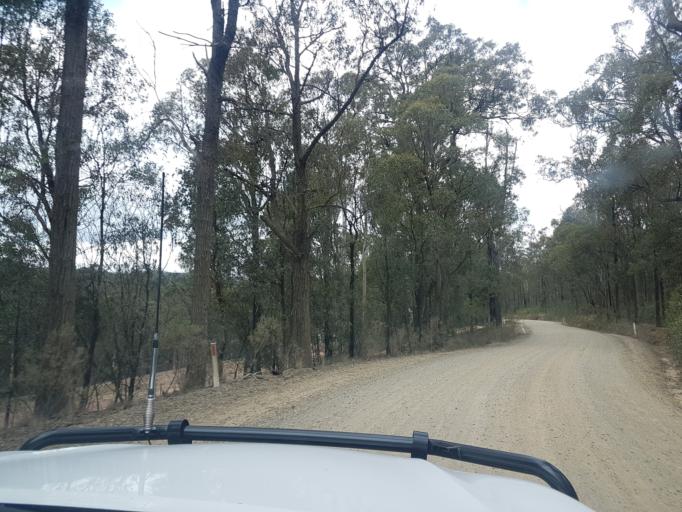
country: AU
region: Victoria
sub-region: East Gippsland
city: Bairnsdale
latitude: -37.6987
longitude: 147.5857
